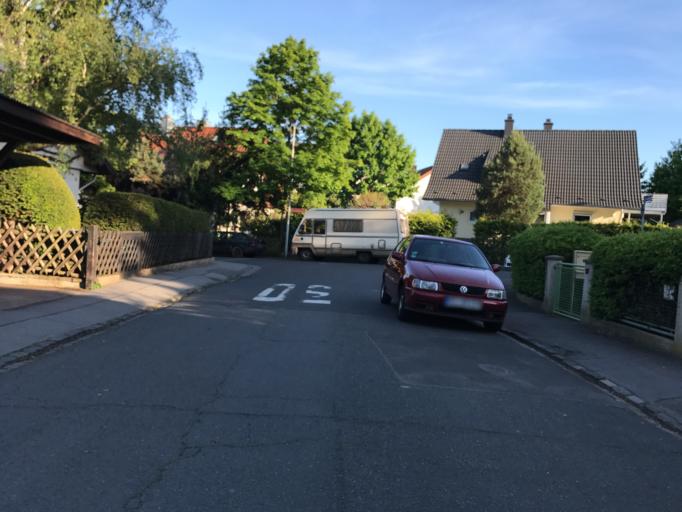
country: DE
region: Rheinland-Pfalz
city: Mainz
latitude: 50.0163
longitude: 8.2281
